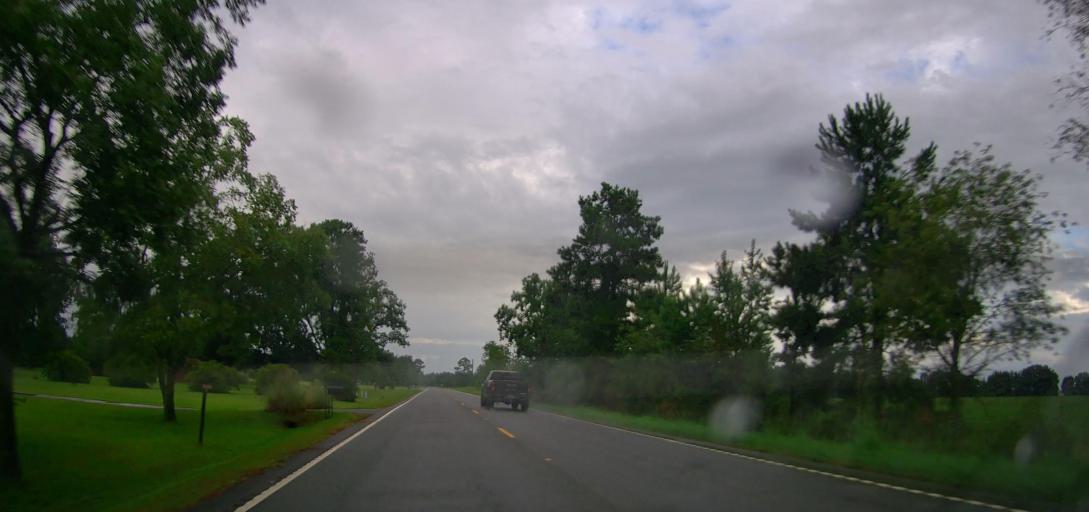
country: US
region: Georgia
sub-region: Ware County
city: Deenwood
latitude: 31.2669
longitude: -82.3982
